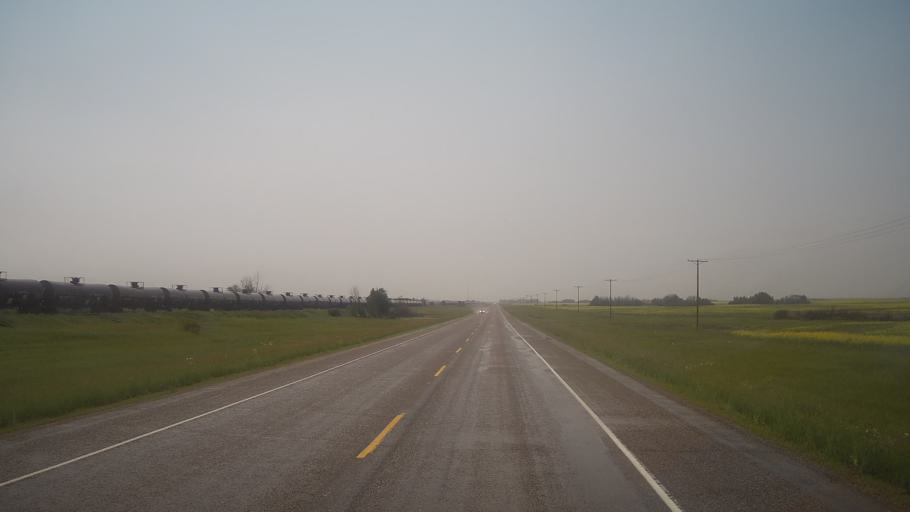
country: CA
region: Saskatchewan
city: Biggar
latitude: 52.1623
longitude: -108.2867
